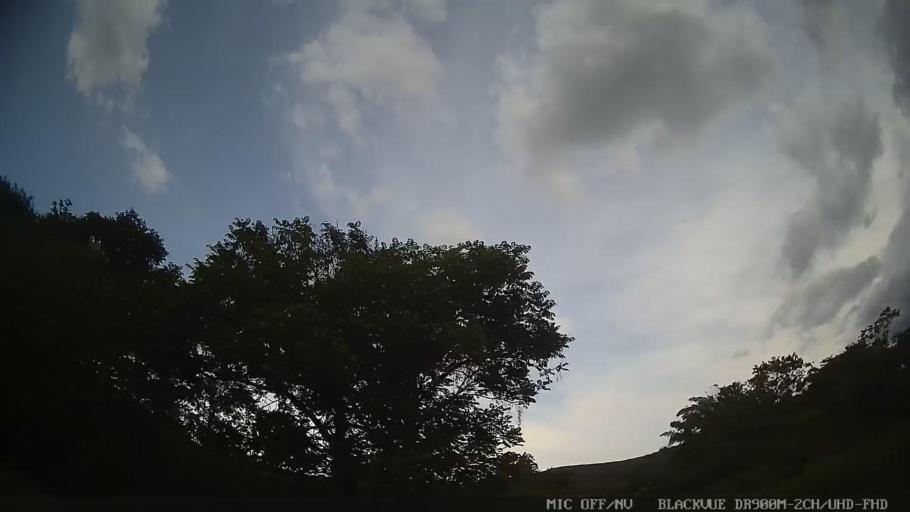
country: BR
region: Sao Paulo
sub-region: Amparo
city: Amparo
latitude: -22.8123
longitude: -46.7554
